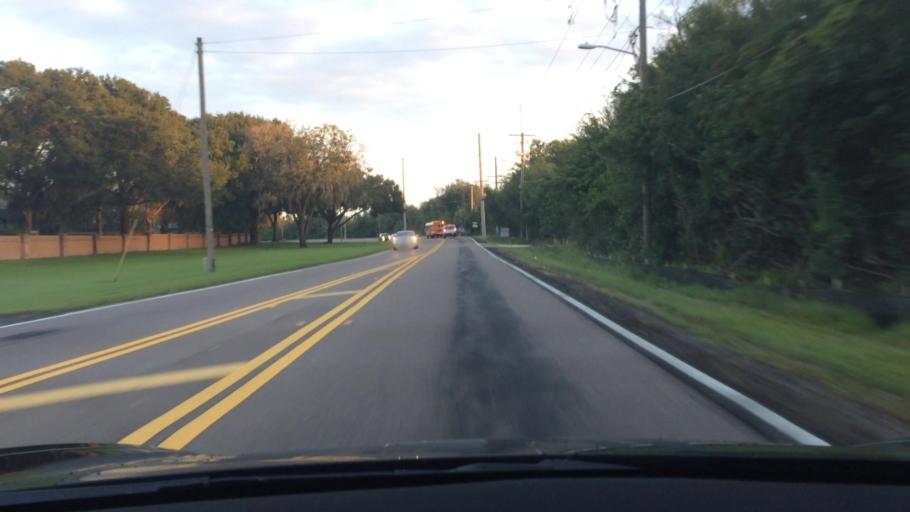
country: US
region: Florida
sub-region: Hillsborough County
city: Citrus Park
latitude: 28.0964
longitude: -82.5791
